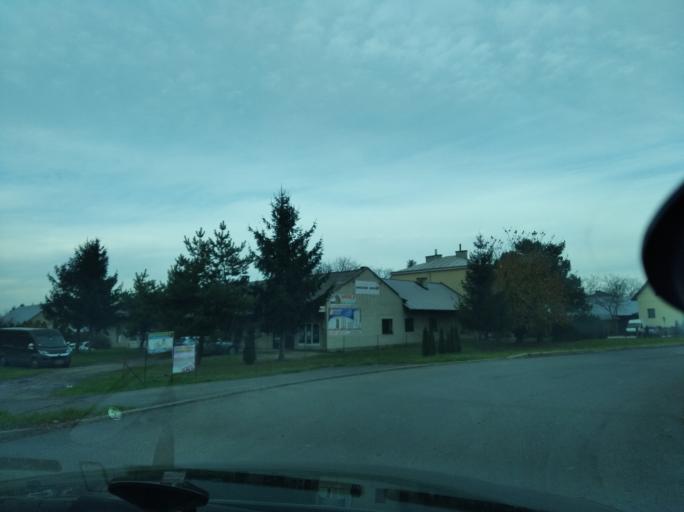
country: PL
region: Subcarpathian Voivodeship
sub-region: Powiat przeworski
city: Przeworsk
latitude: 50.0615
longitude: 22.4733
